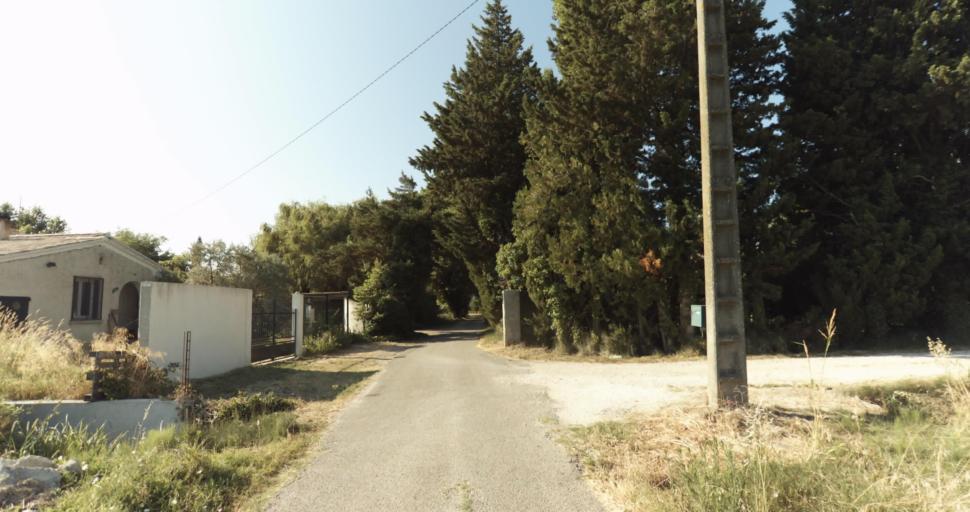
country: FR
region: Provence-Alpes-Cote d'Azur
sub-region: Departement du Vaucluse
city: Monteux
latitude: 44.0476
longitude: 4.9666
